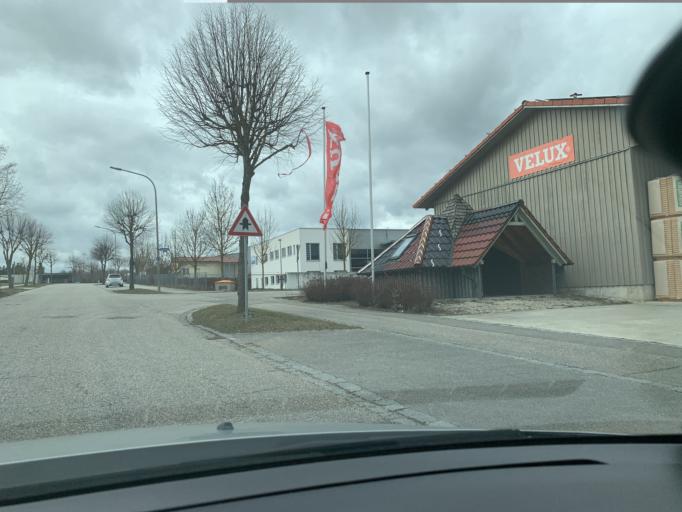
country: DE
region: Bavaria
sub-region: Lower Bavaria
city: Geisenhausen
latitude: 48.4822
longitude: 12.2443
